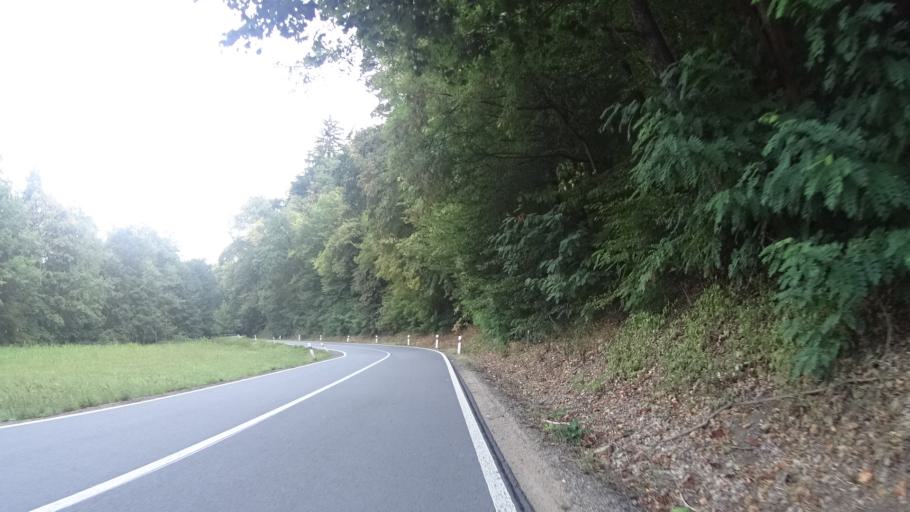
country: CZ
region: Olomoucky
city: Stity
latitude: 49.8678
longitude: 16.7347
